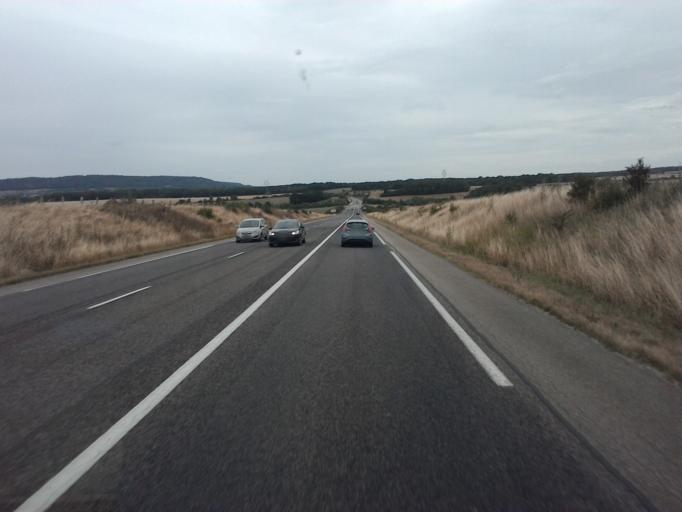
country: FR
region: Lorraine
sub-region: Departement de Meurthe-et-Moselle
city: Bainville-sur-Madon
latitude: 48.5788
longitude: 6.0961
